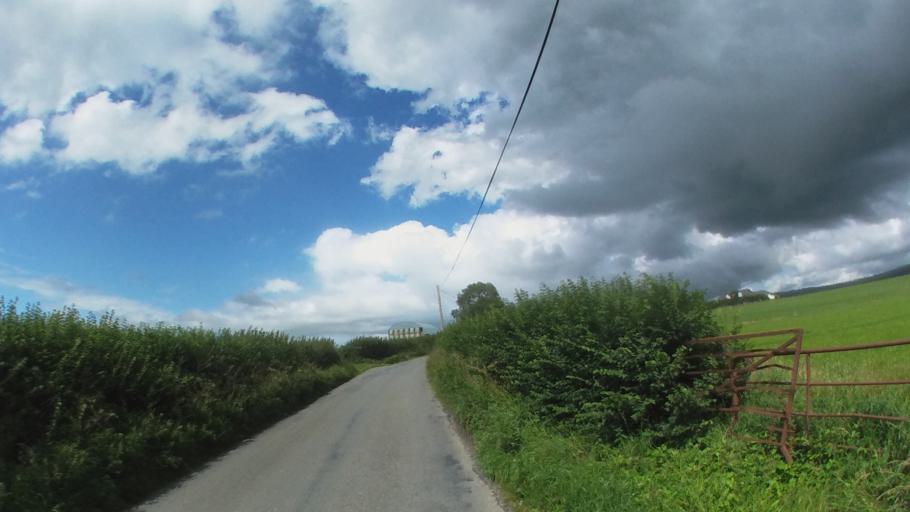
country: IE
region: Leinster
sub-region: Kilkenny
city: Kilkenny
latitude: 52.6887
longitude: -7.2179
